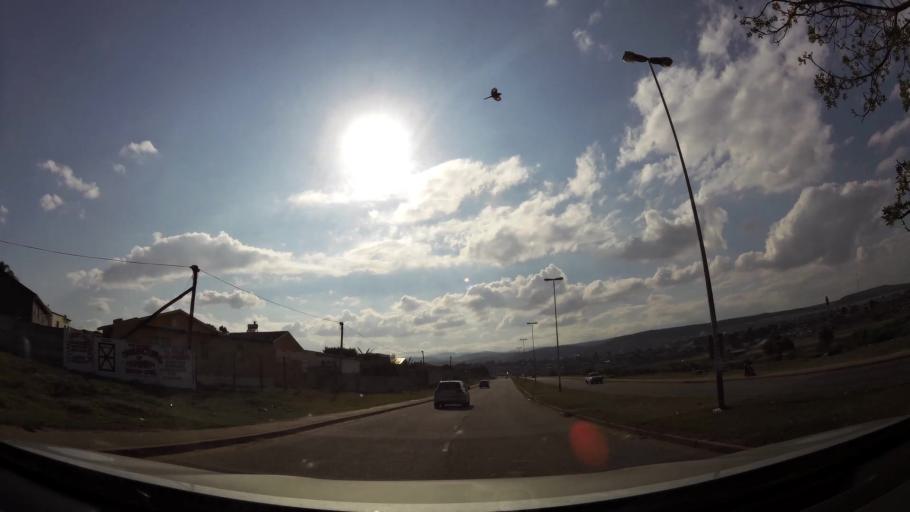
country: ZA
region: Eastern Cape
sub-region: Nelson Mandela Bay Metropolitan Municipality
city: Uitenhage
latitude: -33.7501
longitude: 25.3837
